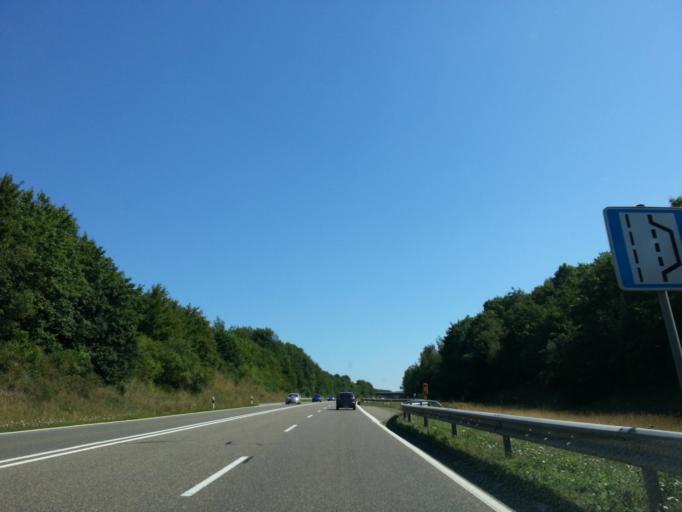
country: DE
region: Rheinland-Pfalz
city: Brandscheid
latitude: 50.2046
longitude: 6.2928
